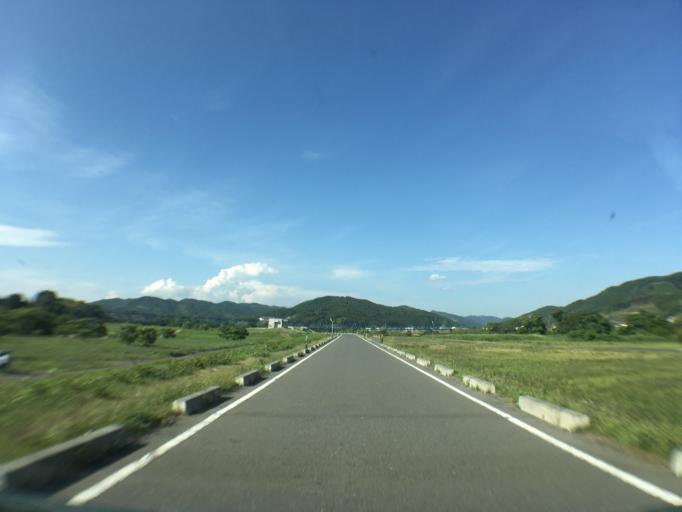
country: JP
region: Miyagi
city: Wakuya
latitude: 38.6048
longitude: 141.2922
